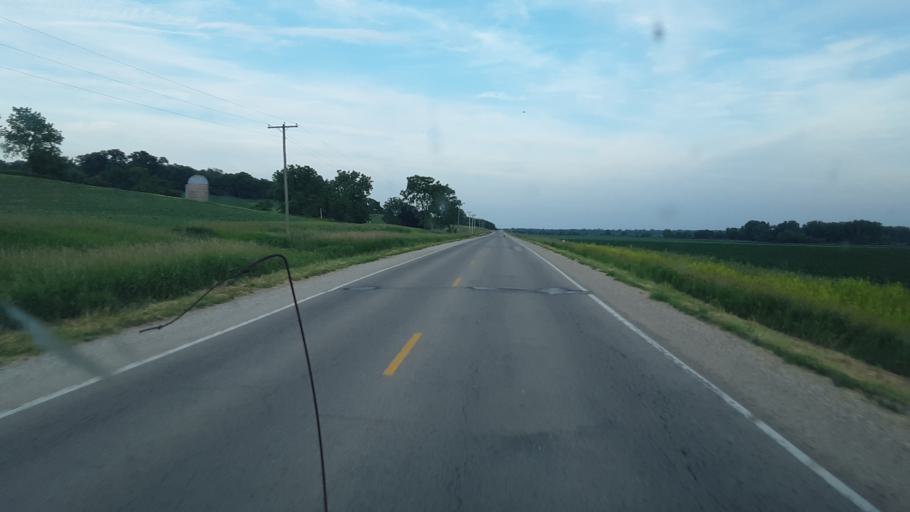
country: US
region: Iowa
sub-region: Benton County
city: Belle Plaine
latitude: 41.9095
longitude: -92.3410
